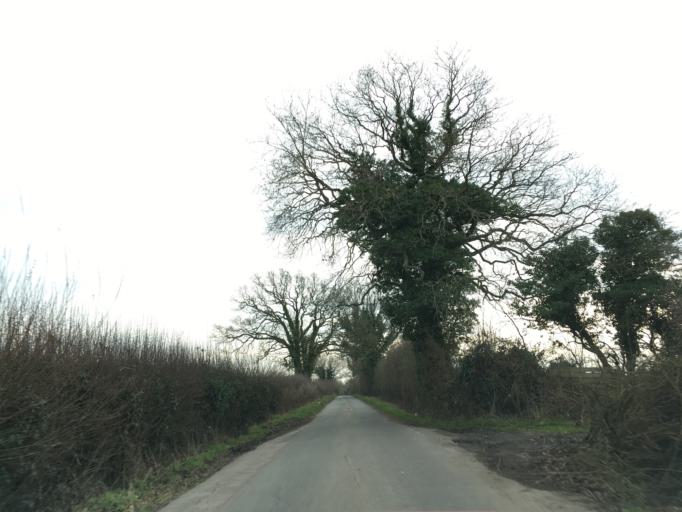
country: GB
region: England
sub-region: South Gloucestershire
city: Yate
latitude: 51.5678
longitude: -2.4250
